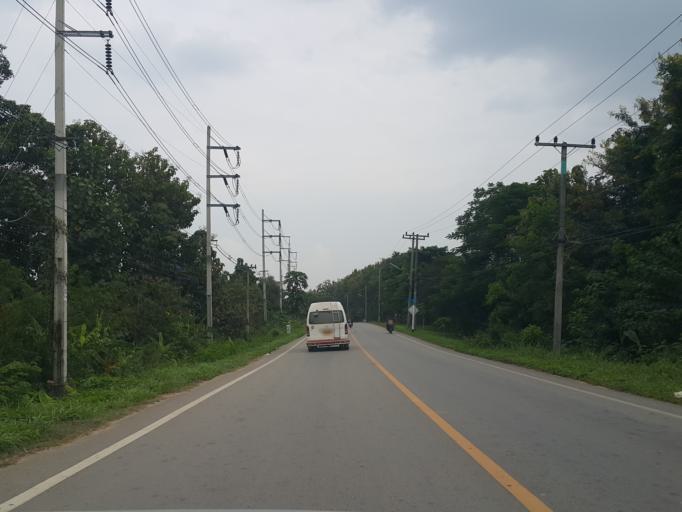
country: TH
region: Chiang Mai
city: Mae Taeng
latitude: 19.0927
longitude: 98.8848
